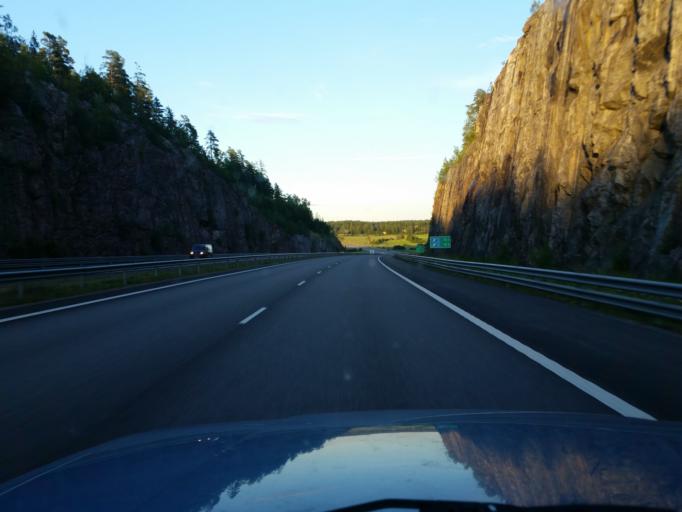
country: FI
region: Varsinais-Suomi
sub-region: Turku
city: Paimio
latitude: 60.4269
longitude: 22.7381
